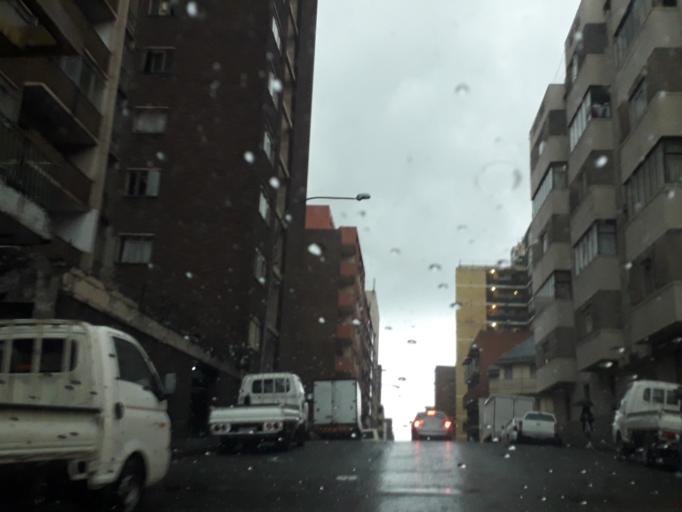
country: ZA
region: Gauteng
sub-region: City of Johannesburg Metropolitan Municipality
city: Johannesburg
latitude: -26.1884
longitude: 28.0499
